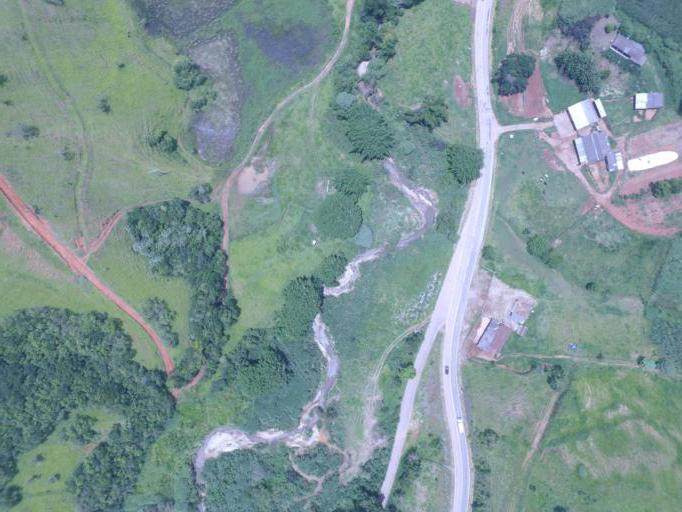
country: BR
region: Minas Gerais
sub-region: Tiradentes
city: Tiradentes
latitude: -21.0908
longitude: -44.0729
